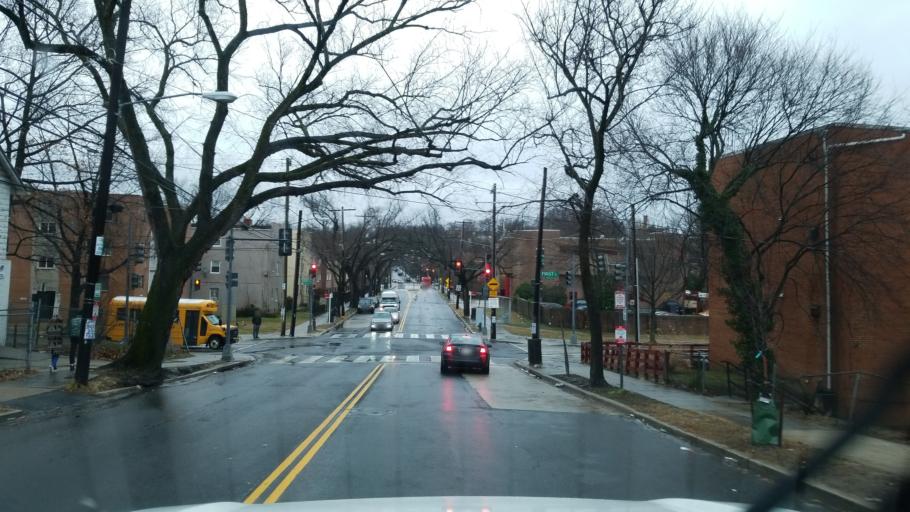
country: US
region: Maryland
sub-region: Prince George's County
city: Glassmanor
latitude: 38.8312
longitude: -77.0064
